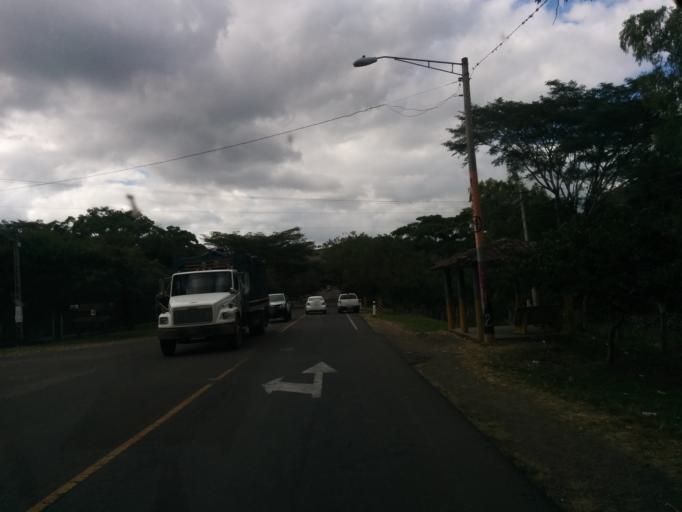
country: NI
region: Esteli
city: Esteli
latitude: 13.0005
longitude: -86.3049
